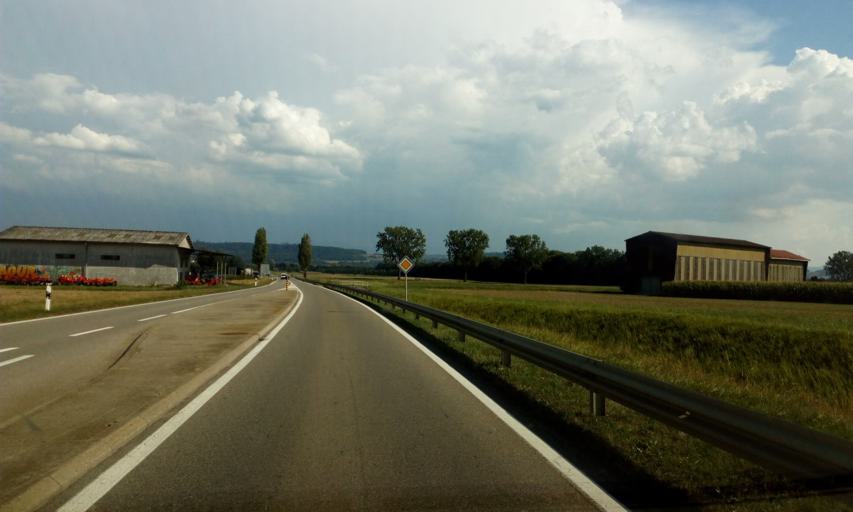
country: CH
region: Fribourg
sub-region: Broye District
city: Domdidier
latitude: 46.9001
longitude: 6.9933
